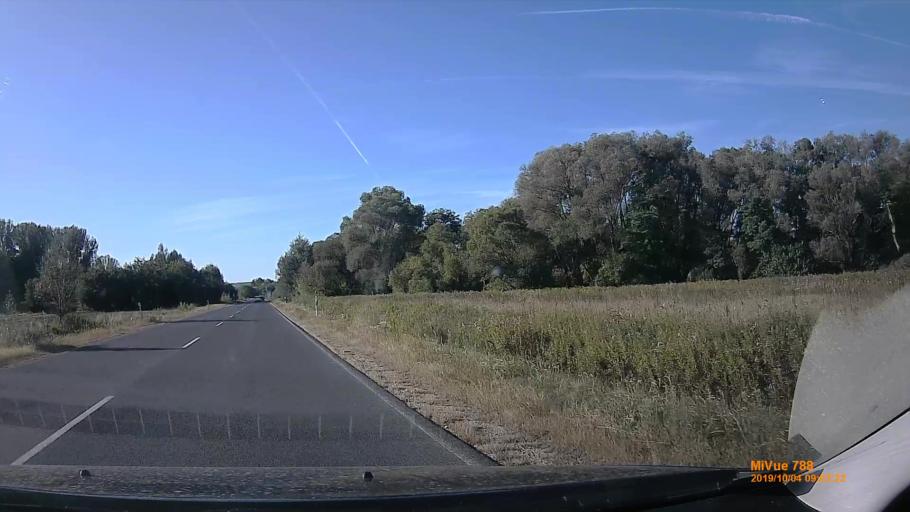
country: HU
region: Somogy
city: Karad
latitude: 46.7119
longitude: 17.7731
